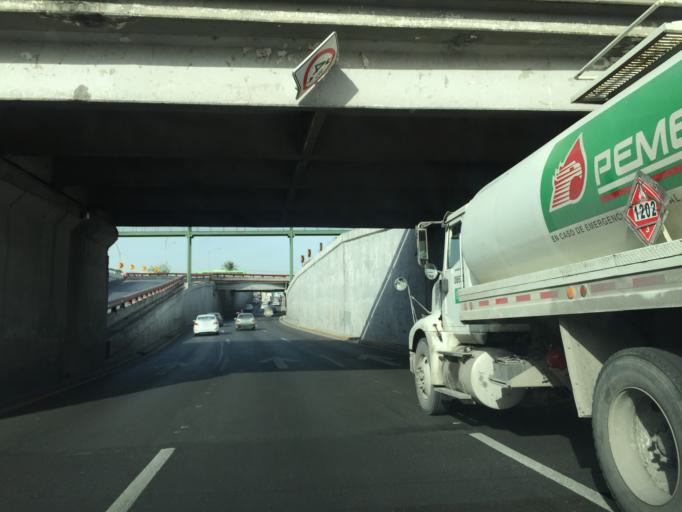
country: MX
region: Nuevo Leon
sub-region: Monterrey
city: Monterrey
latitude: 25.6653
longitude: -100.3193
